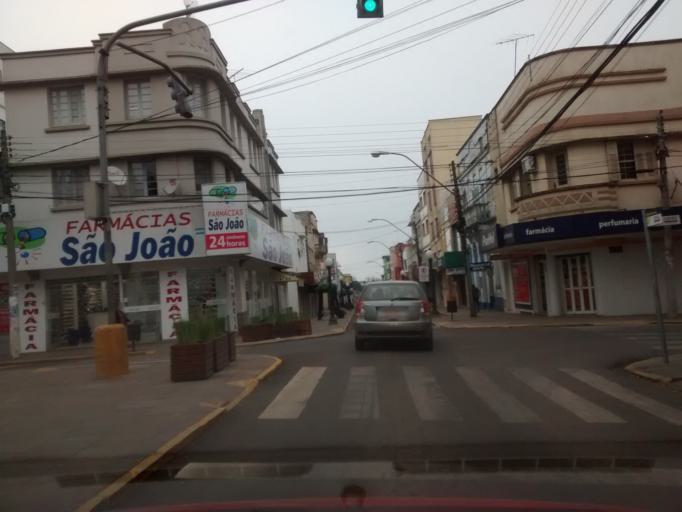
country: BR
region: Rio Grande do Sul
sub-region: Vacaria
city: Vacaria
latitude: -28.5037
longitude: -50.9380
